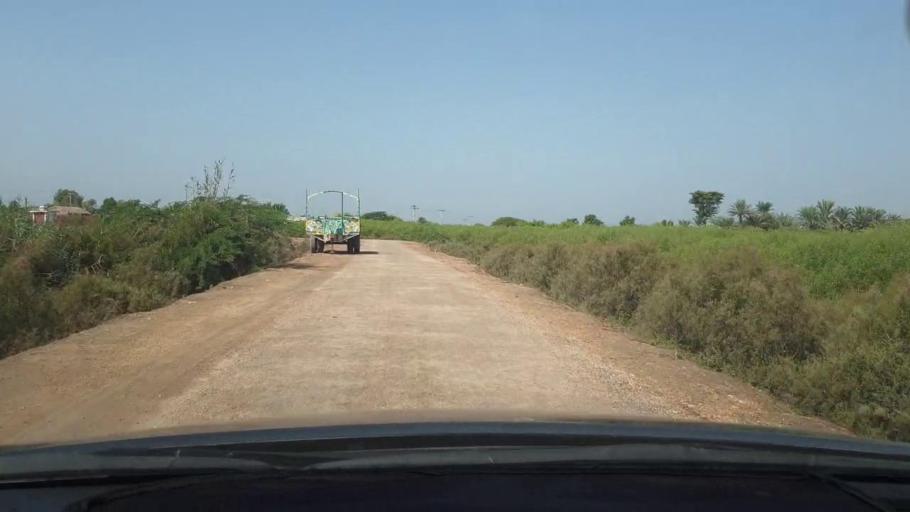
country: PK
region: Sindh
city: Tando Bago
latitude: 24.6891
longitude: 69.1243
